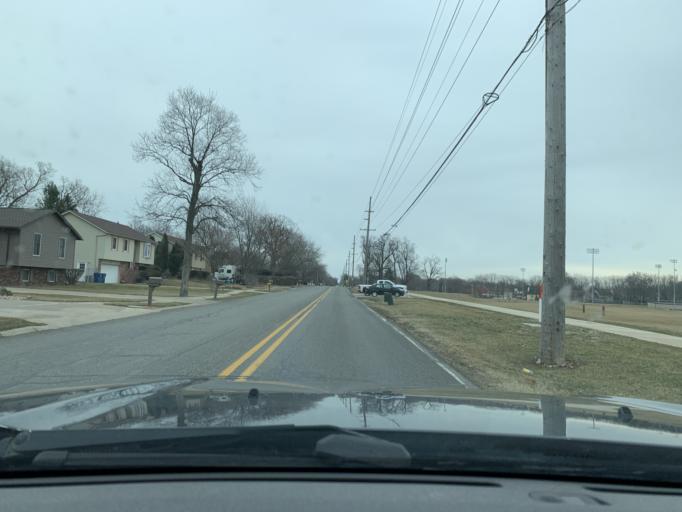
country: US
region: Indiana
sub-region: Porter County
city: Chesterton
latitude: 41.5936
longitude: -87.0664
